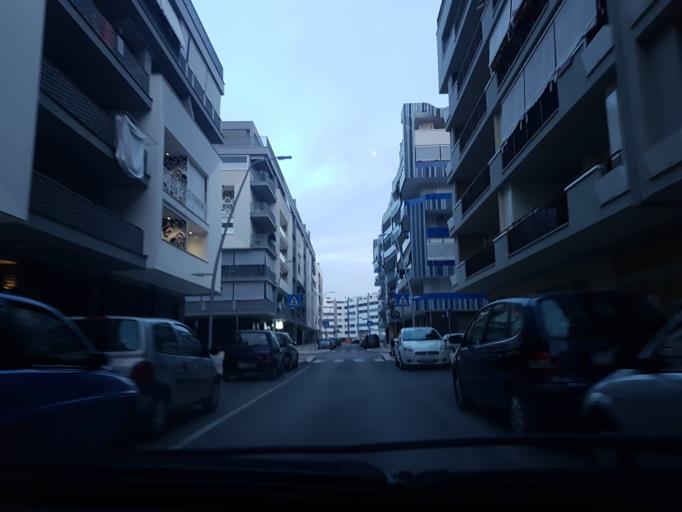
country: IT
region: Apulia
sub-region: Provincia di Barletta - Andria - Trani
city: Barletta
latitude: 41.3054
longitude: 16.2659
